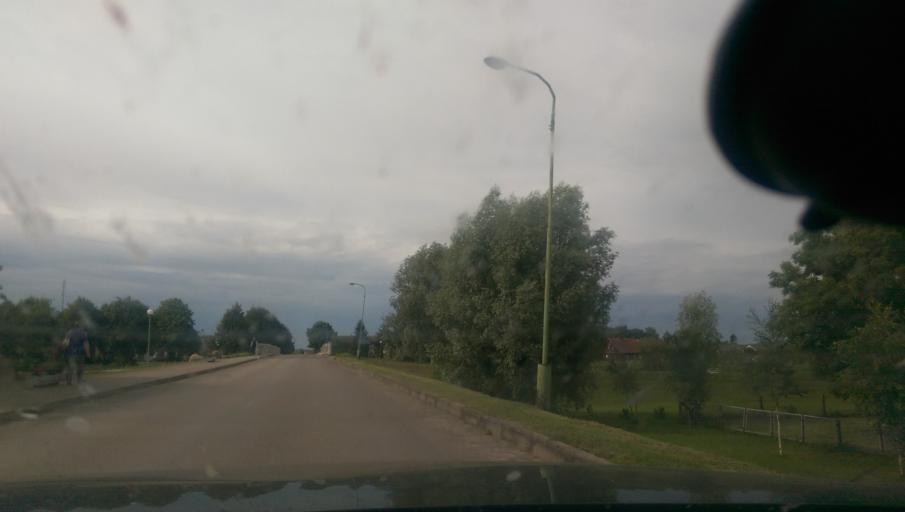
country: LT
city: Rusne
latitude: 55.2961
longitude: 21.3745
